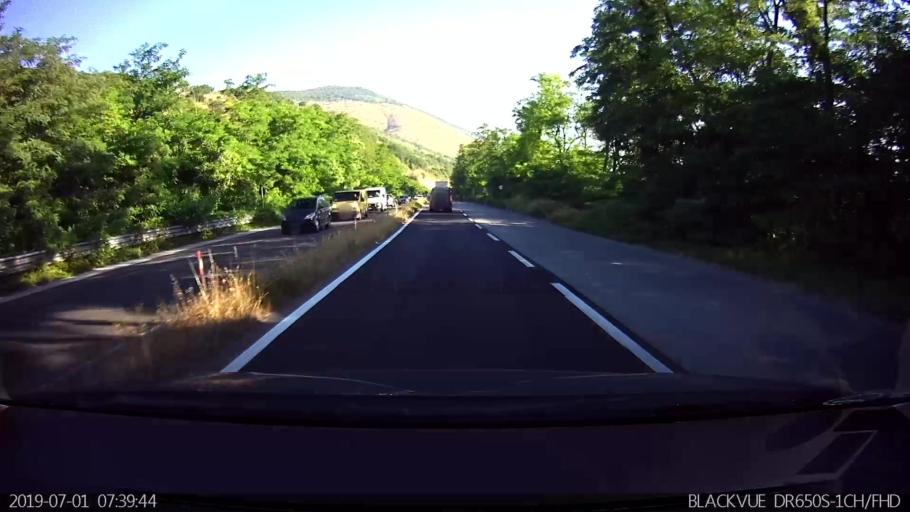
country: IT
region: Latium
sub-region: Provincia di Frosinone
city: Giuliano di Roma
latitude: 41.5518
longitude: 13.2676
